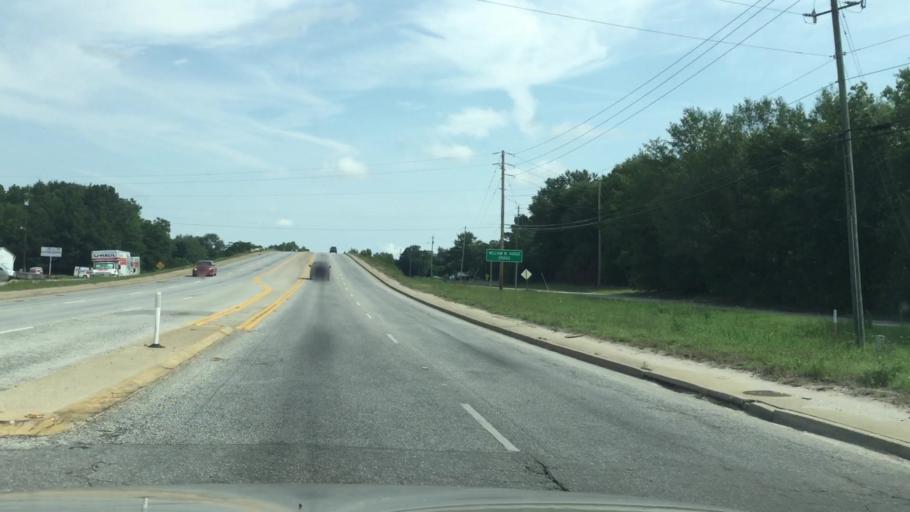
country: US
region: South Carolina
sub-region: Sumter County
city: South Sumter
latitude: 33.9031
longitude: -80.3537
